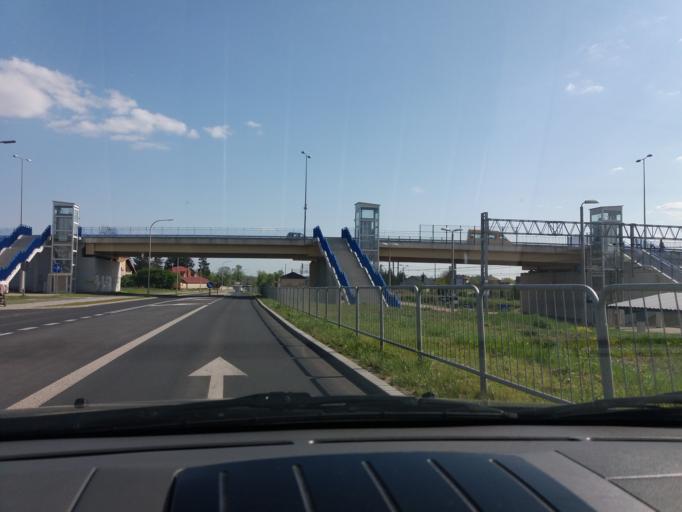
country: PL
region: Masovian Voivodeship
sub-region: Powiat mlawski
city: Mlawa
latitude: 53.1093
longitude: 20.3642
